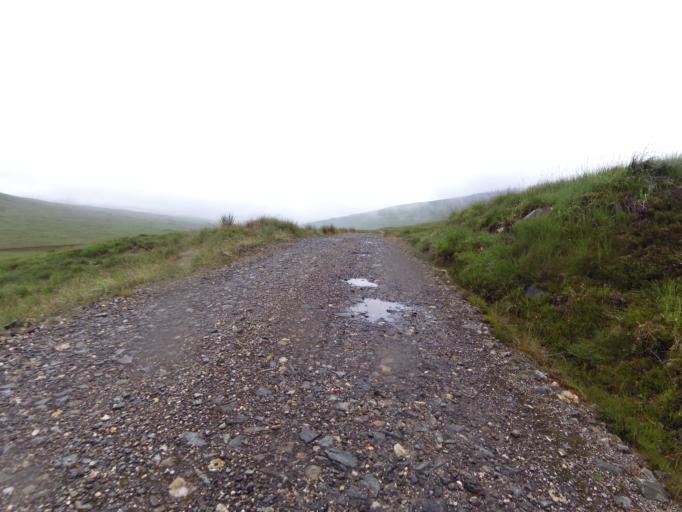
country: GB
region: Scotland
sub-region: Highland
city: Spean Bridge
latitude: 56.7703
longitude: -4.6977
